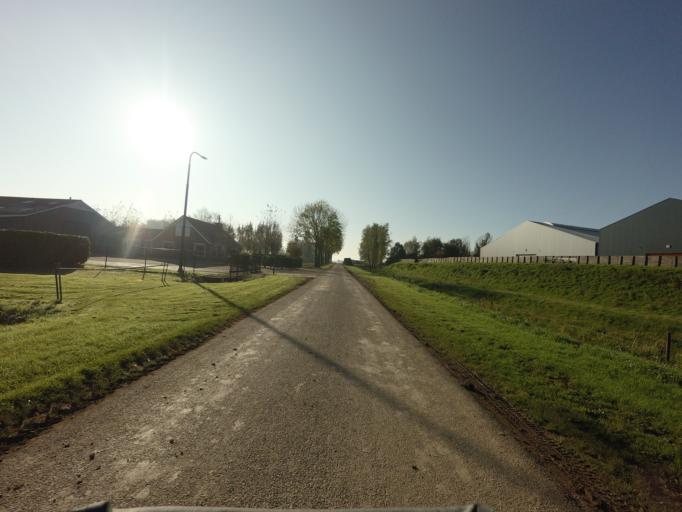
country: NL
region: North Brabant
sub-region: Gemeente Werkendam
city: Werkendam
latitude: 51.7986
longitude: 4.8850
